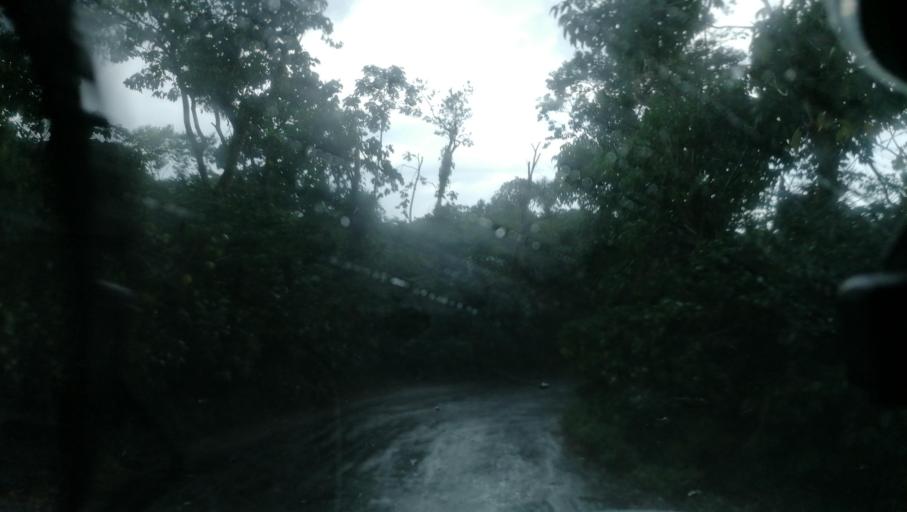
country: MX
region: Chiapas
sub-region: Cacahoatan
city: Benito Juarez
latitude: 15.0685
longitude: -92.1910
